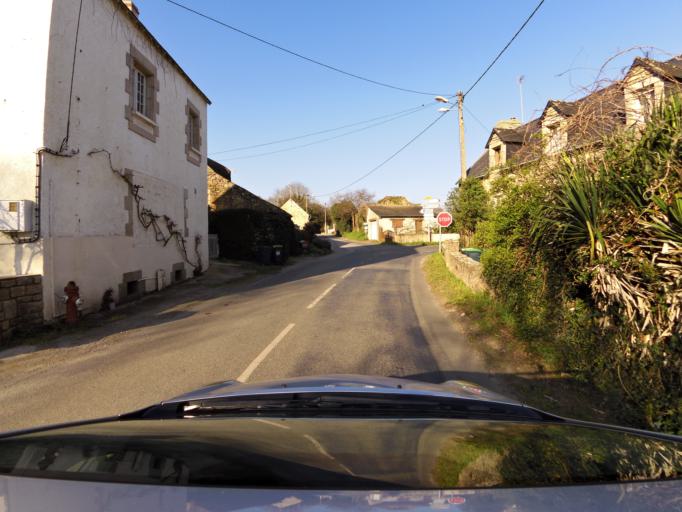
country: FR
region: Brittany
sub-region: Departement du Morbihan
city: Ploemeur
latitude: 47.7475
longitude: -3.4754
